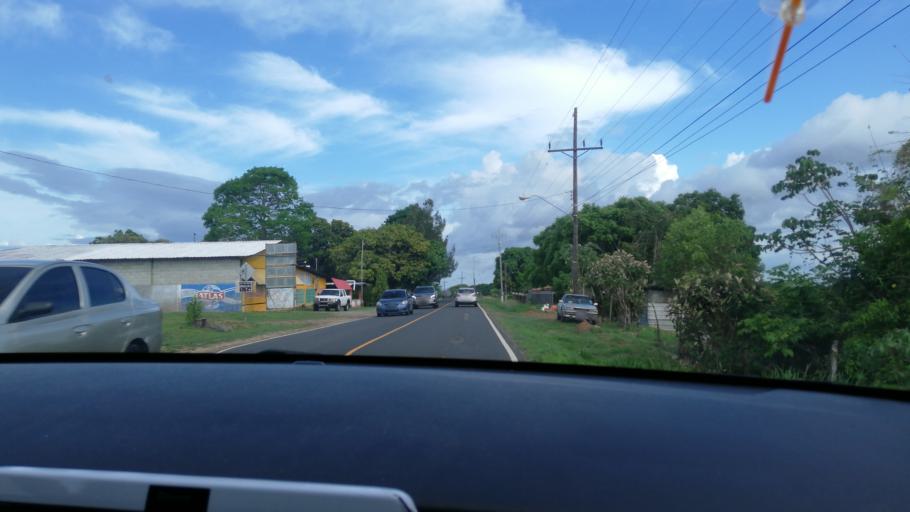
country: PA
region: Panama
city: Las Colinas
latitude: 8.5184
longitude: -80.0364
